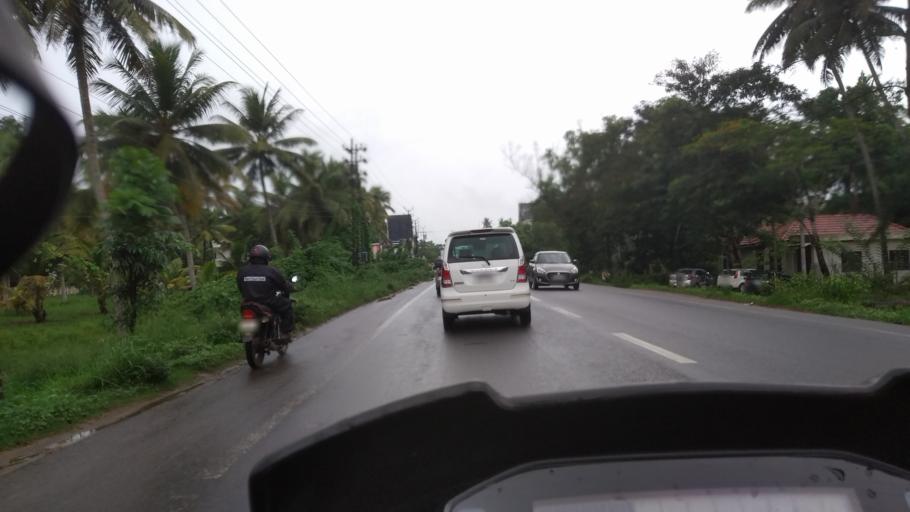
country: IN
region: Kerala
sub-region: Alappuzha
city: Kayankulam
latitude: 9.1236
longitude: 76.5175
